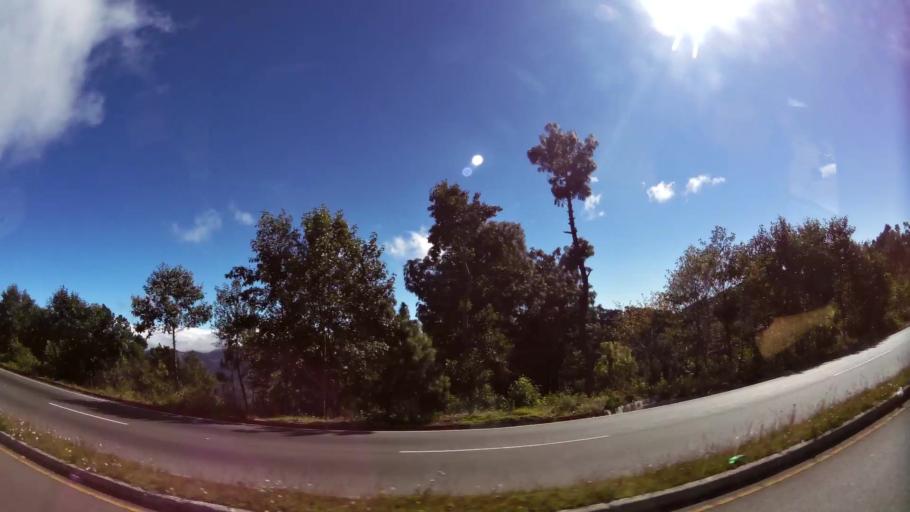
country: GT
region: Solola
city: Santa Catarina Ixtahuacan
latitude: 14.8297
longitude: -91.3625
